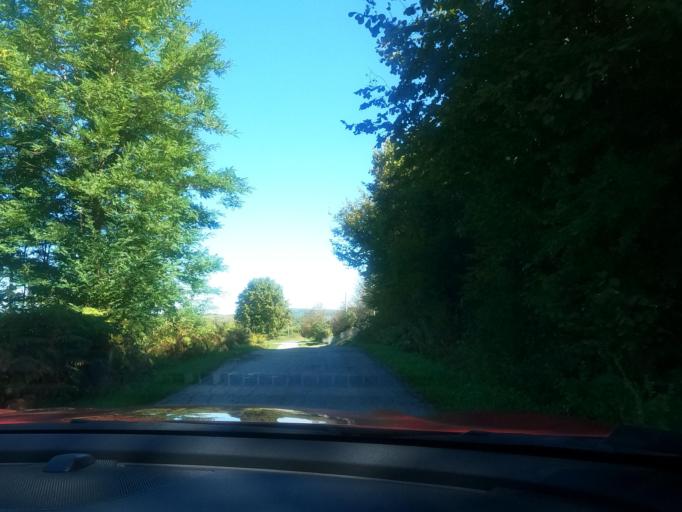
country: HR
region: Sisacko-Moslavacka
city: Petrinja
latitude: 45.3527
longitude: 16.2167
